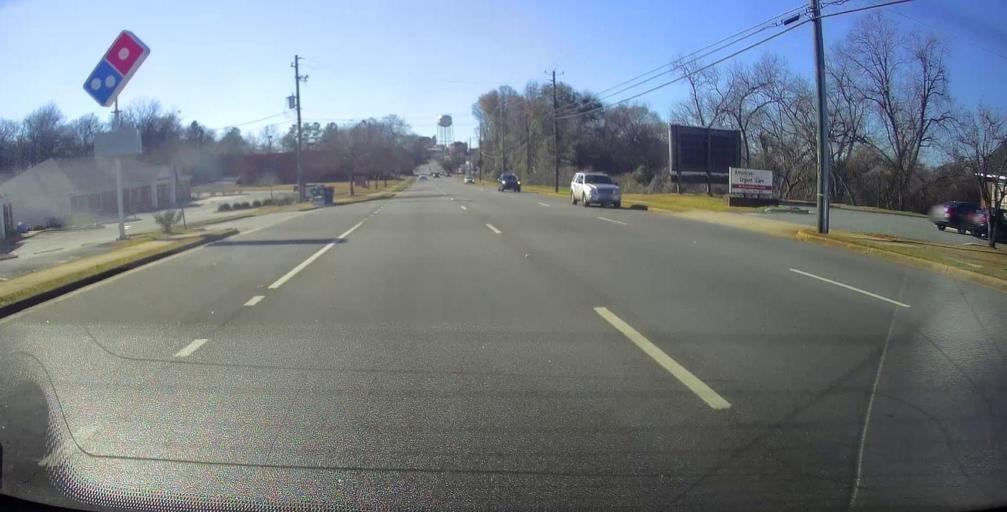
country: US
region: Georgia
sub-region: Sumter County
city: Americus
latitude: 32.0716
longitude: -84.2250
